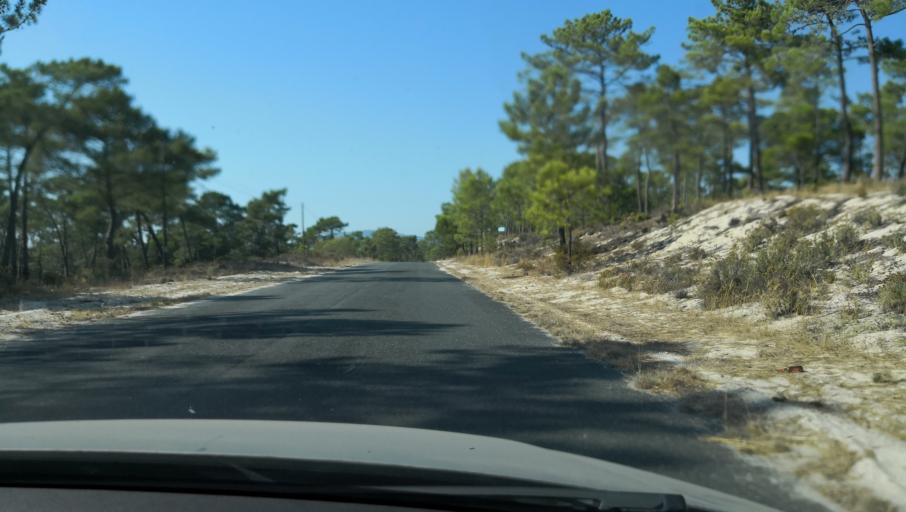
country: PT
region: Setubal
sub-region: Setubal
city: Setubal
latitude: 38.4711
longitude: -8.8724
